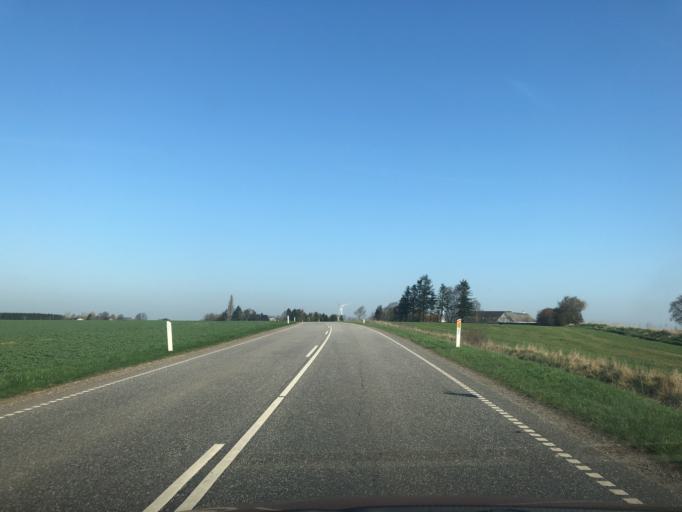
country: DK
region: Zealand
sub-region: Faxe Kommune
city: Haslev
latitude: 55.3487
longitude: 11.9377
